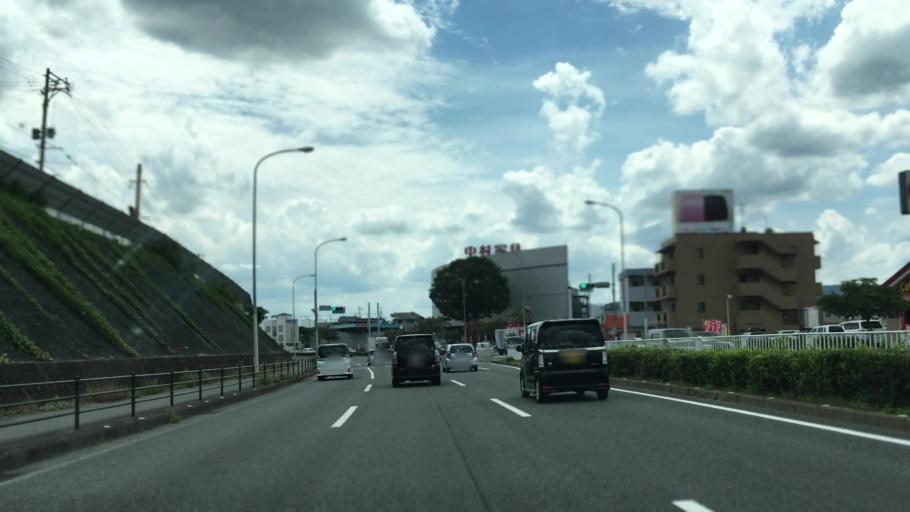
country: JP
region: Fukuoka
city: Dazaifu
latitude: 33.5007
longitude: 130.5314
